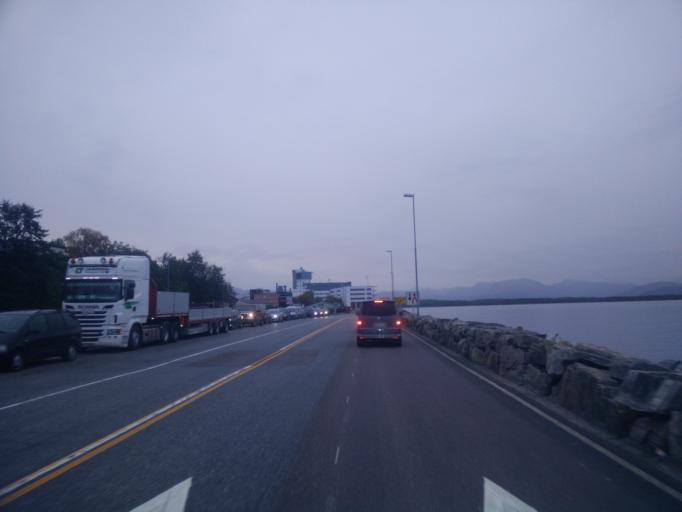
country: NO
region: More og Romsdal
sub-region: Molde
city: Molde
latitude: 62.7369
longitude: 7.1721
